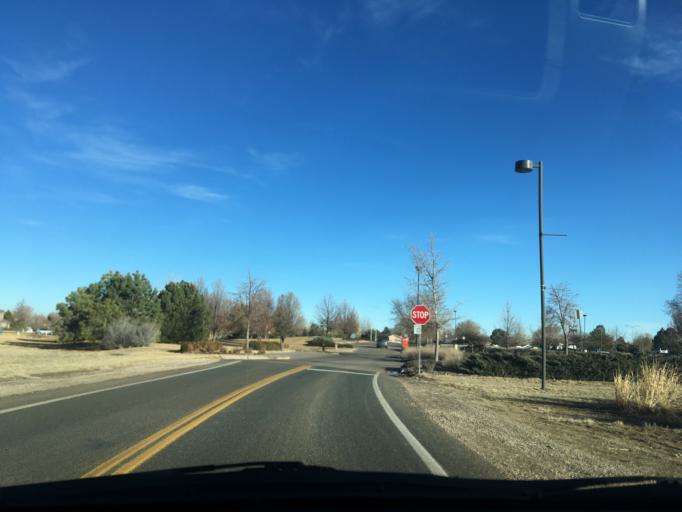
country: US
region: Colorado
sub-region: Broomfield County
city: Broomfield
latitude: 39.9358
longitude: -105.0364
